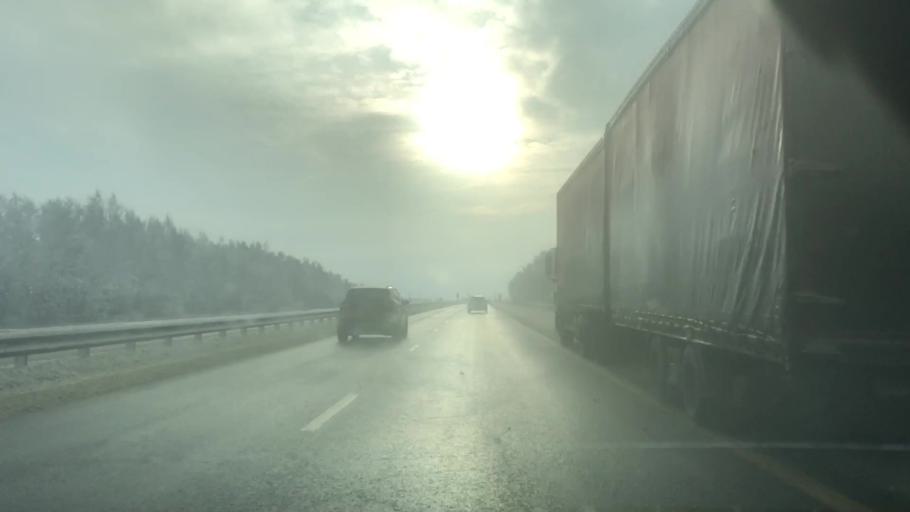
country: RU
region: Tula
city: Venev
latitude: 54.2861
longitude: 38.1589
